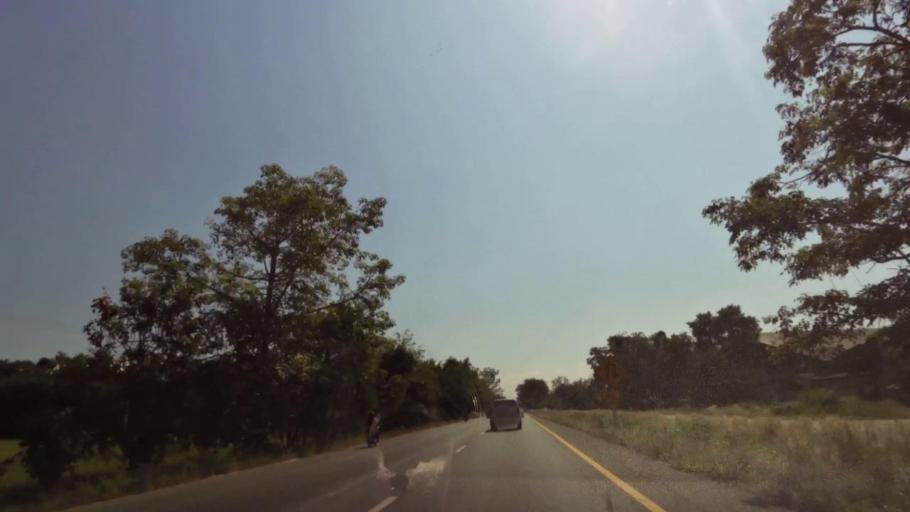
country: TH
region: Nakhon Sawan
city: Kao Liao
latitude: 15.8534
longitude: 100.1172
